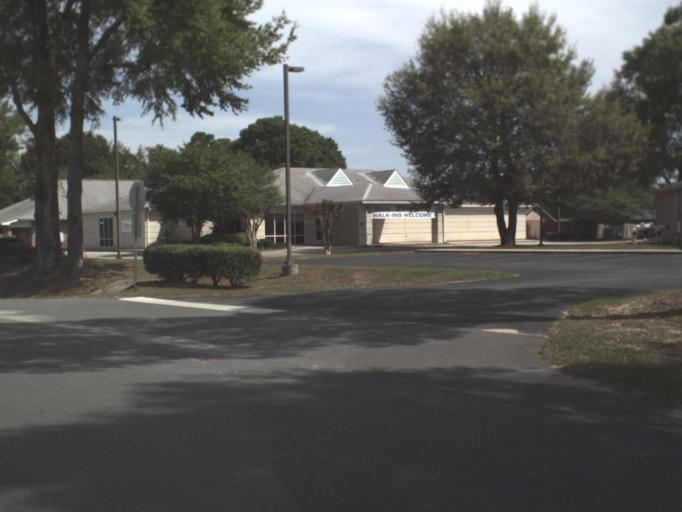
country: US
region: Florida
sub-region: Santa Rosa County
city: Pace
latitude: 30.6037
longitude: -87.1392
